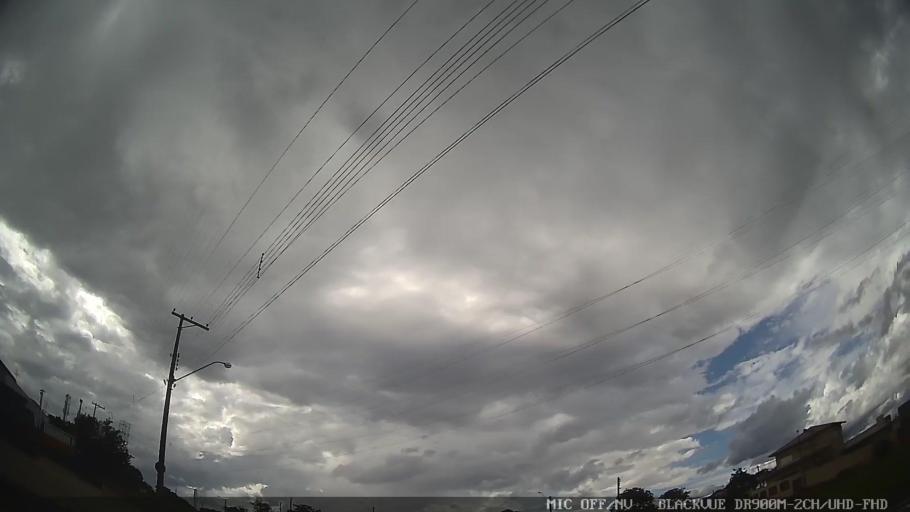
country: BR
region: Sao Paulo
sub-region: Jaguariuna
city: Jaguariuna
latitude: -22.6825
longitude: -46.9918
